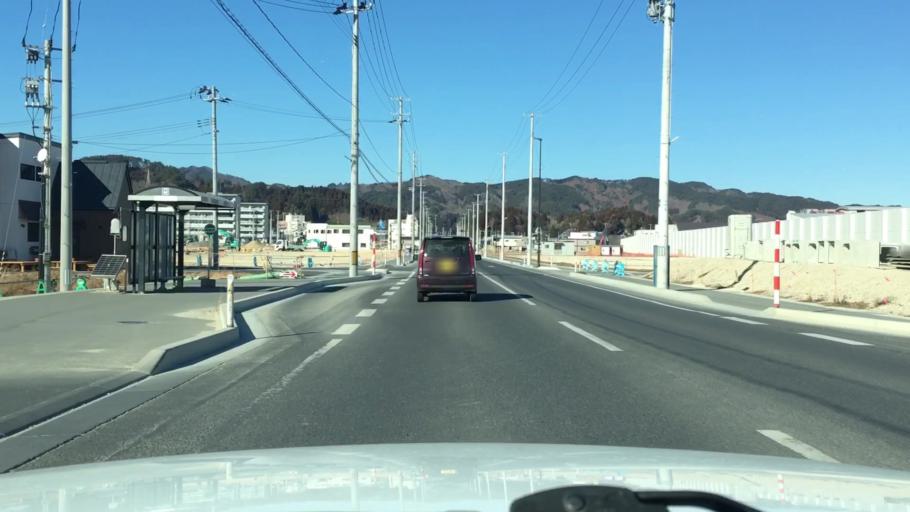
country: JP
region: Iwate
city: Yamada
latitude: 39.4610
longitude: 141.9555
